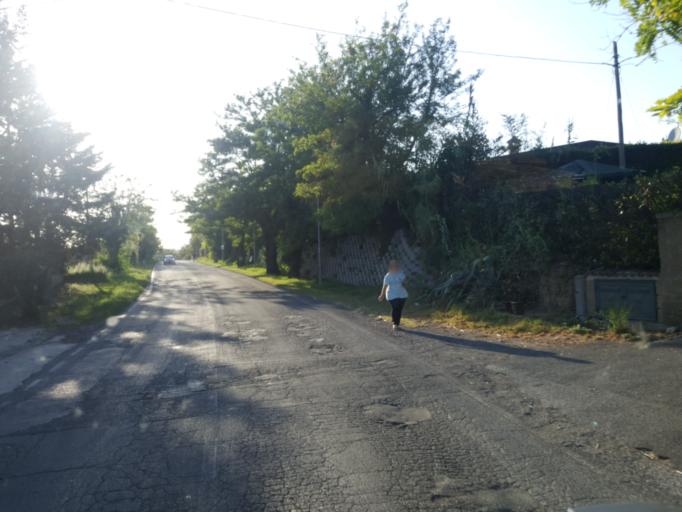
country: IT
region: Latium
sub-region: Citta metropolitana di Roma Capitale
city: Bivio di Capanelle
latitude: 42.1239
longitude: 12.5827
